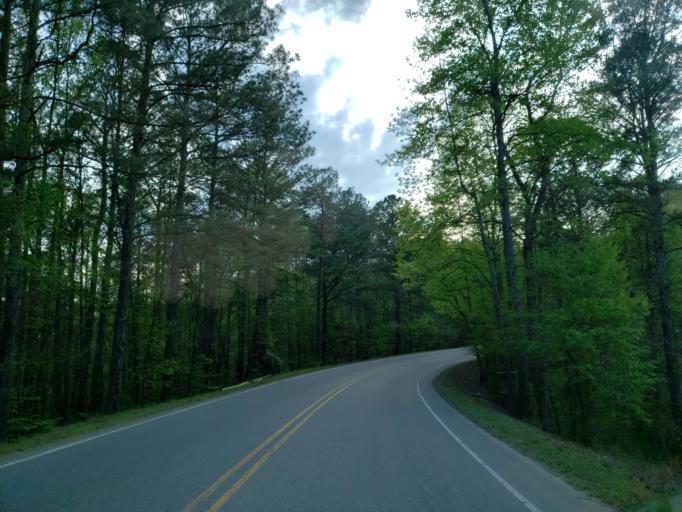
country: US
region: Georgia
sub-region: Cherokee County
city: Ball Ground
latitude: 34.2941
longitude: -84.3926
